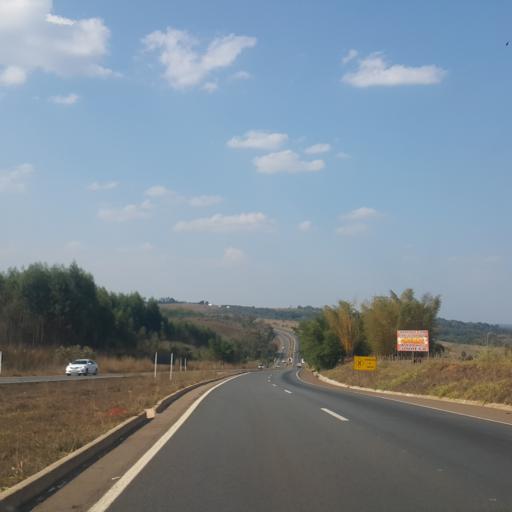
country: BR
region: Goias
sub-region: Abadiania
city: Abadiania
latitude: -16.2998
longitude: -48.8099
